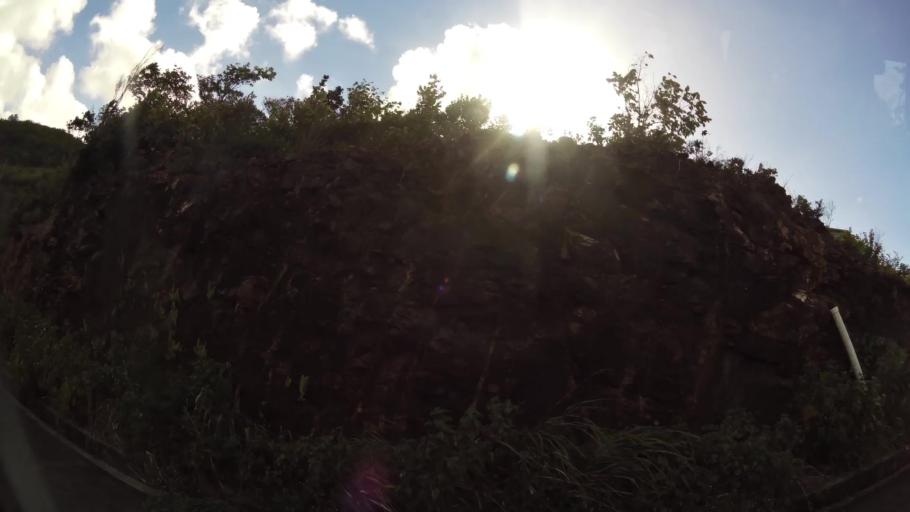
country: LC
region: Castries Quarter
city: Bisee
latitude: 14.0400
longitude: -60.9571
